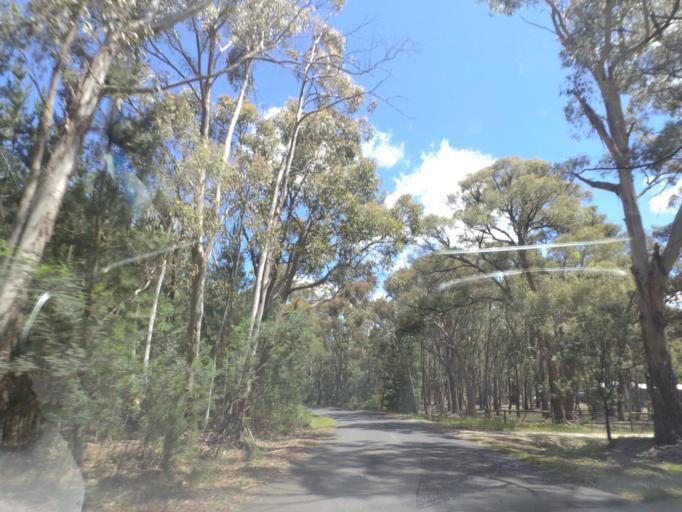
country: AU
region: Victoria
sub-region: Mount Alexander
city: Castlemaine
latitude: -37.3015
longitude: 144.1884
